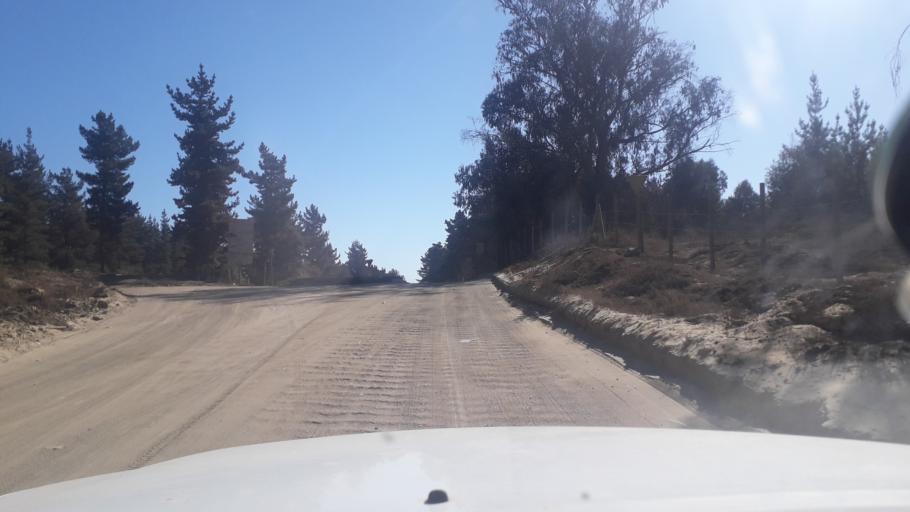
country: CL
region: Valparaiso
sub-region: Provincia de Valparaiso
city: Vina del Mar
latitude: -32.9542
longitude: -71.5283
